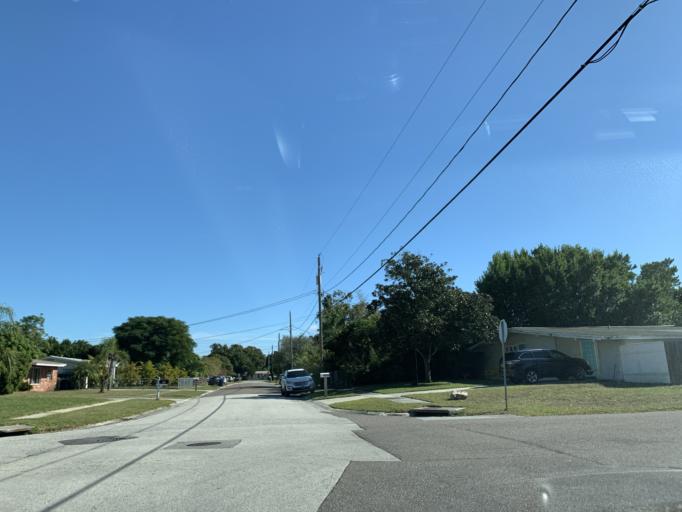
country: US
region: Florida
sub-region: Hillsborough County
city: Tampa
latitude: 27.8860
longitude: -82.5044
